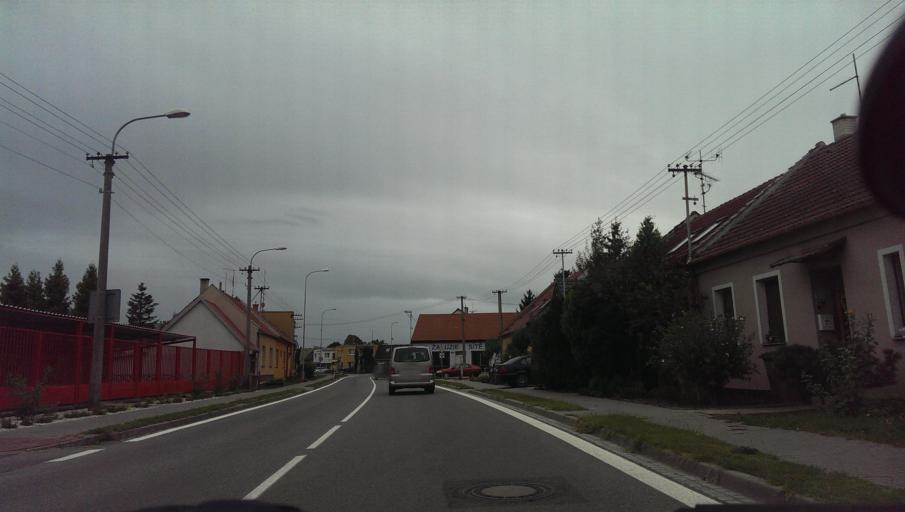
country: CZ
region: South Moravian
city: Bzenec
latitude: 48.9731
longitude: 17.2539
